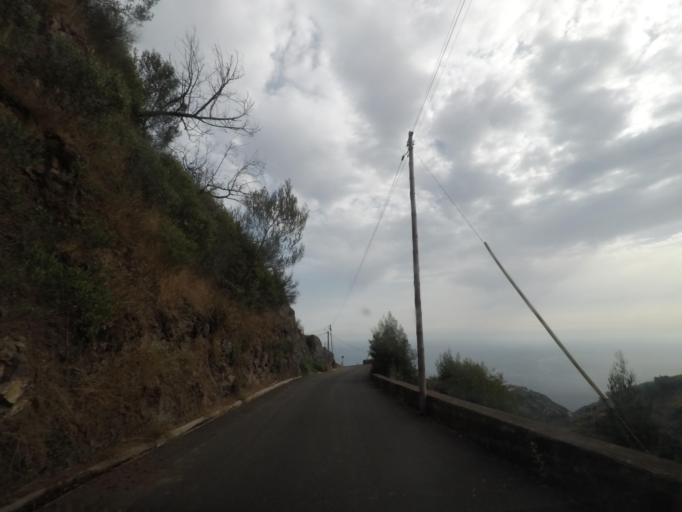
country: PT
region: Madeira
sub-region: Calheta
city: Arco da Calheta
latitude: 32.7377
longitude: -17.1538
